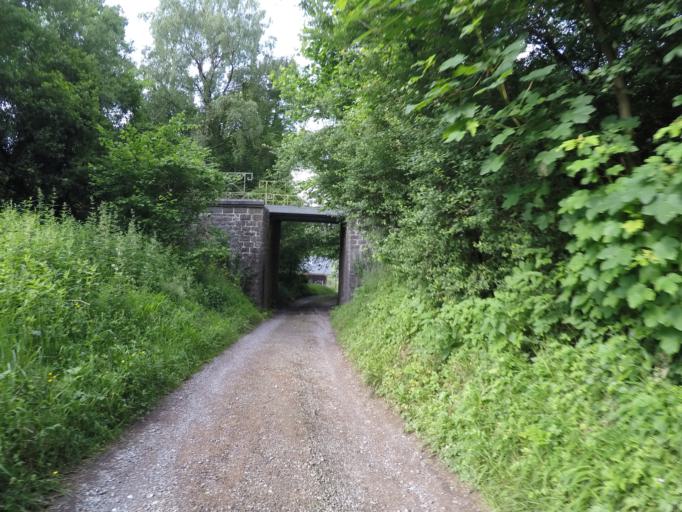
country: BE
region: Wallonia
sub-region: Province de Namur
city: Assesse
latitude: 50.3165
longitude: 5.0243
